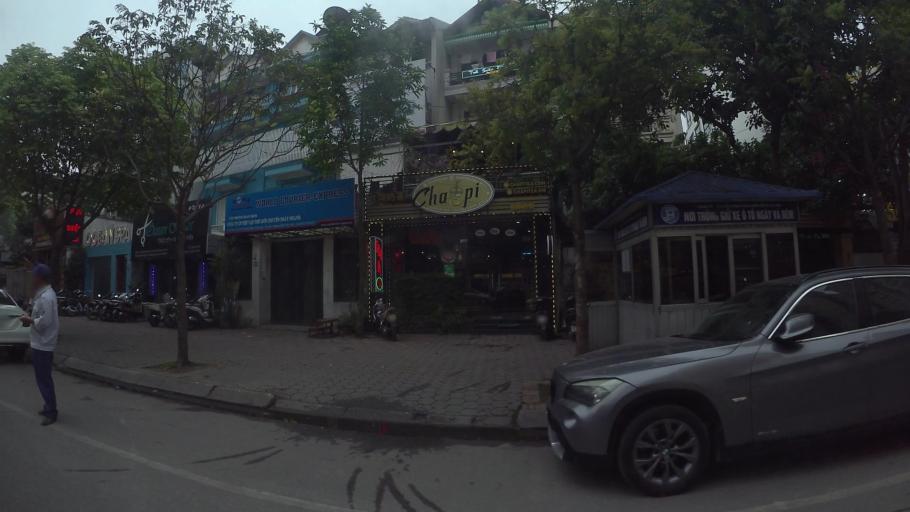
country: VN
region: Ha Noi
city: Cau Giay
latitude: 21.0189
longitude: 105.7996
